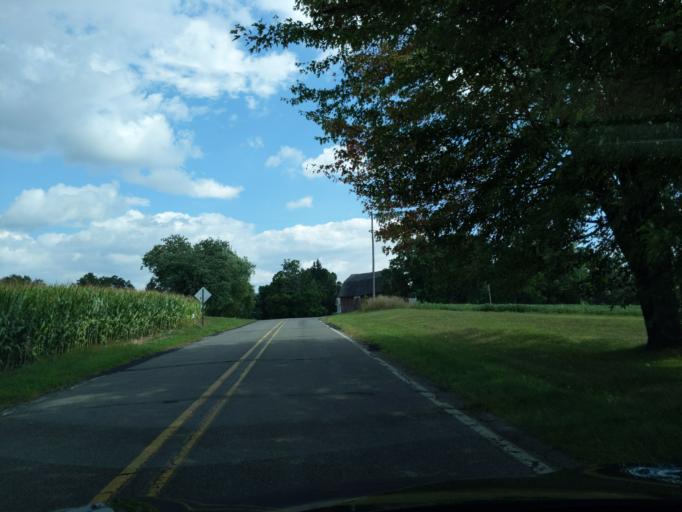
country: US
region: Michigan
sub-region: Jackson County
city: Spring Arbor
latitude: 42.3266
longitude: -84.5377
